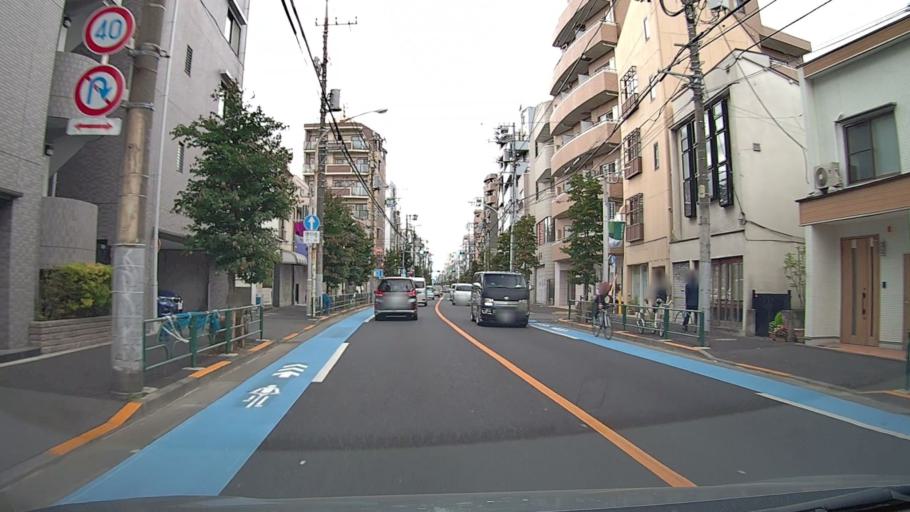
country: JP
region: Tokyo
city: Tokyo
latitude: 35.7099
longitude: 139.6491
